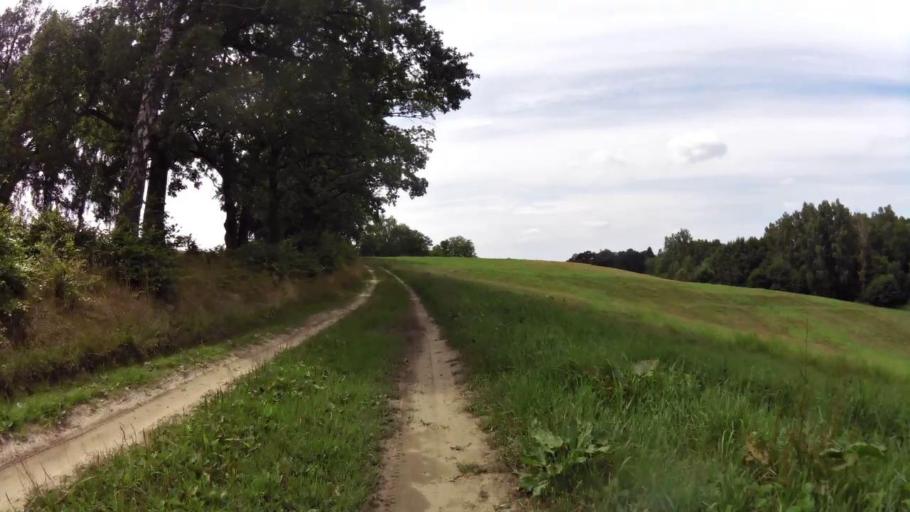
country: PL
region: West Pomeranian Voivodeship
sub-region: Powiat drawski
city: Drawsko Pomorskie
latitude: 53.5041
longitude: 15.6870
